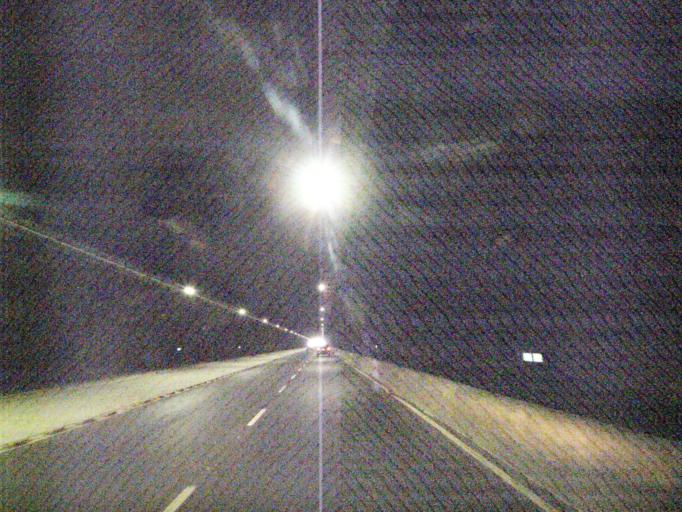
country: BR
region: Rio de Janeiro
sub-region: Niteroi
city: Niteroi
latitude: -22.9338
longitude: -43.0926
